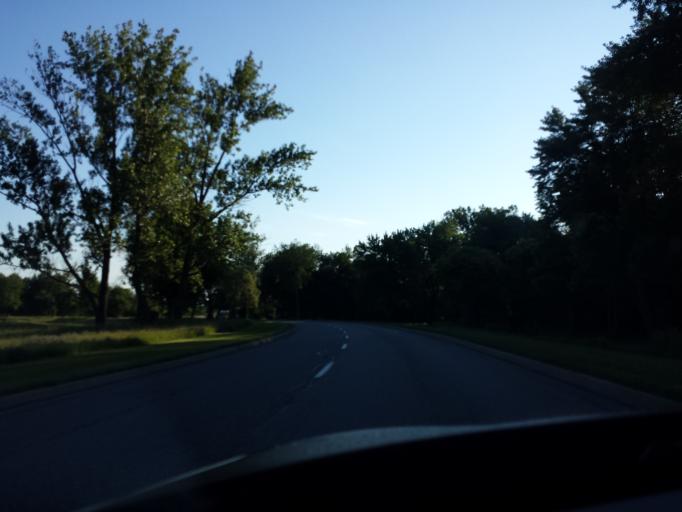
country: CA
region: Ontario
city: Bells Corners
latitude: 45.3762
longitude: -75.7800
